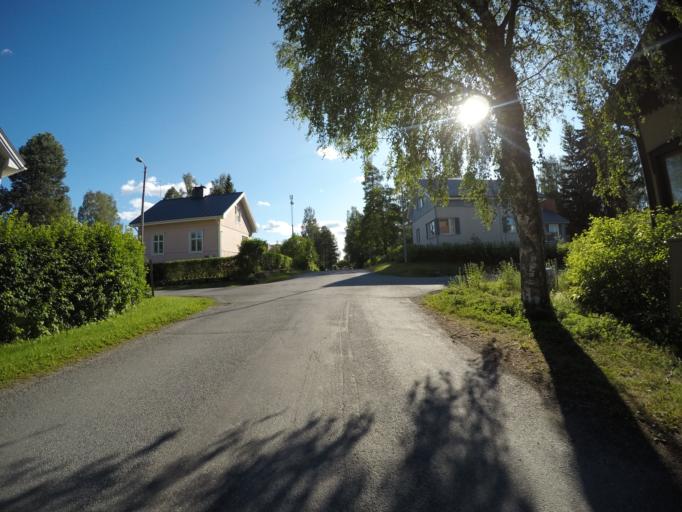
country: FI
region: Haeme
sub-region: Haemeenlinna
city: Haemeenlinna
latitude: 61.0077
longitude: 24.4842
